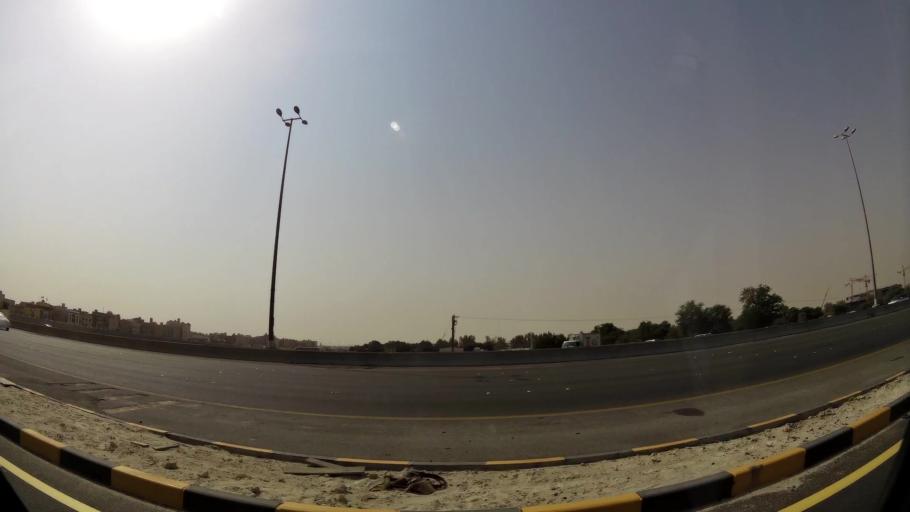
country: KW
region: Muhafazat al Jahra'
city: Al Jahra'
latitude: 29.3310
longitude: 47.7351
